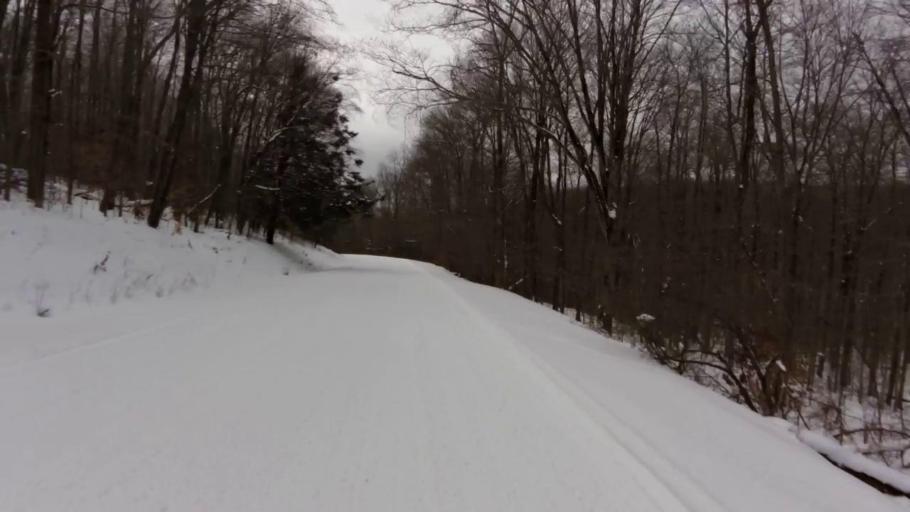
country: US
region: New York
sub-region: Cattaraugus County
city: Salamanca
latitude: 42.0396
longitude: -78.7847
